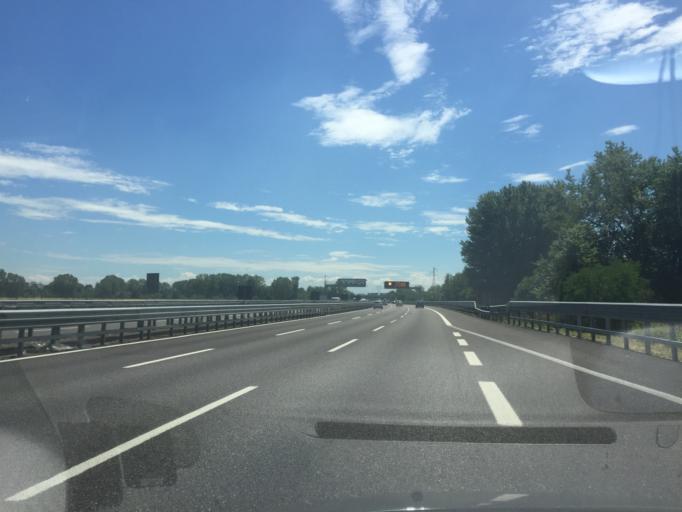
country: IT
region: Lombardy
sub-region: Citta metropolitana di Milano
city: Cesano Boscone
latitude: 45.4428
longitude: 9.0736
